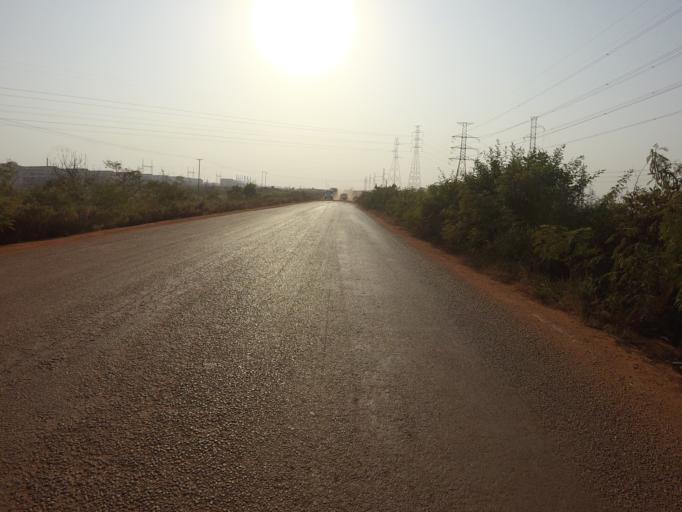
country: GH
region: Greater Accra
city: Tema
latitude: 5.6727
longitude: 0.0241
